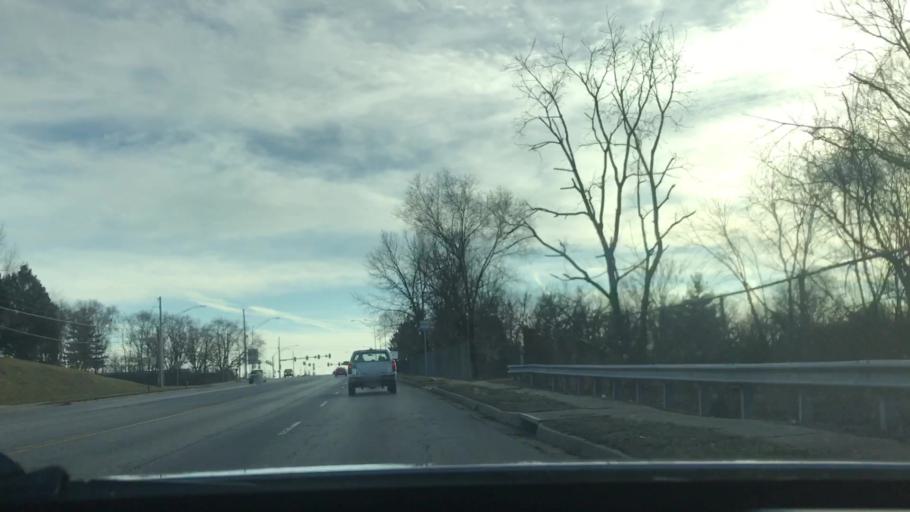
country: US
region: Missouri
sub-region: Jackson County
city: Independence
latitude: 39.0367
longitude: -94.3880
